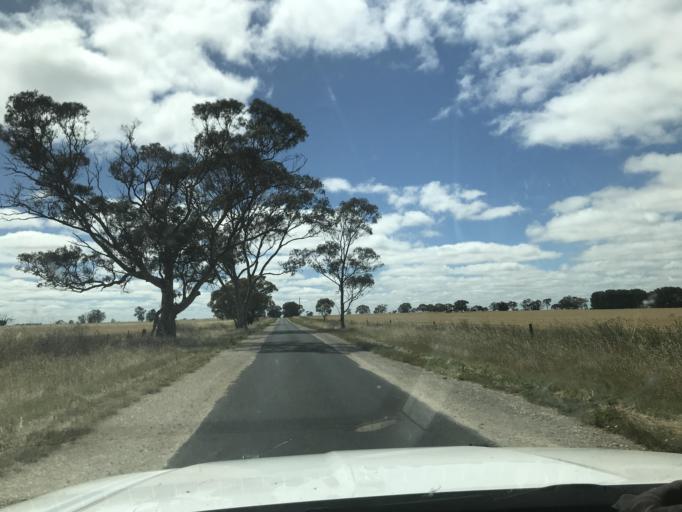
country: AU
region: South Australia
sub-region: Tatiara
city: Bordertown
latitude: -36.2788
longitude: 141.1186
